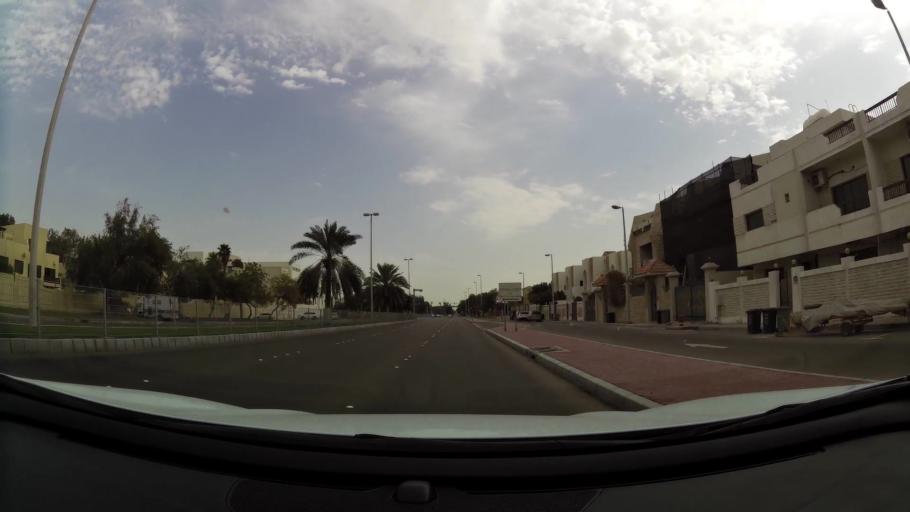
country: AE
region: Abu Dhabi
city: Abu Dhabi
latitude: 24.4605
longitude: 54.3710
